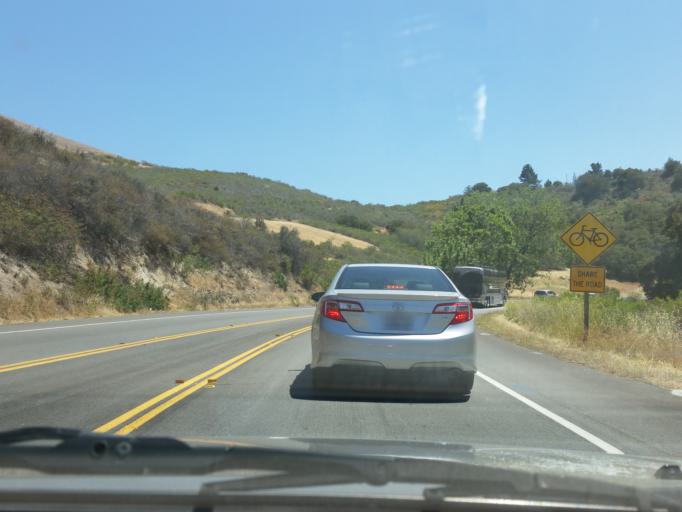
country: US
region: California
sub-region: San Luis Obispo County
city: Avila Beach
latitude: 35.1822
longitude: -120.7232
